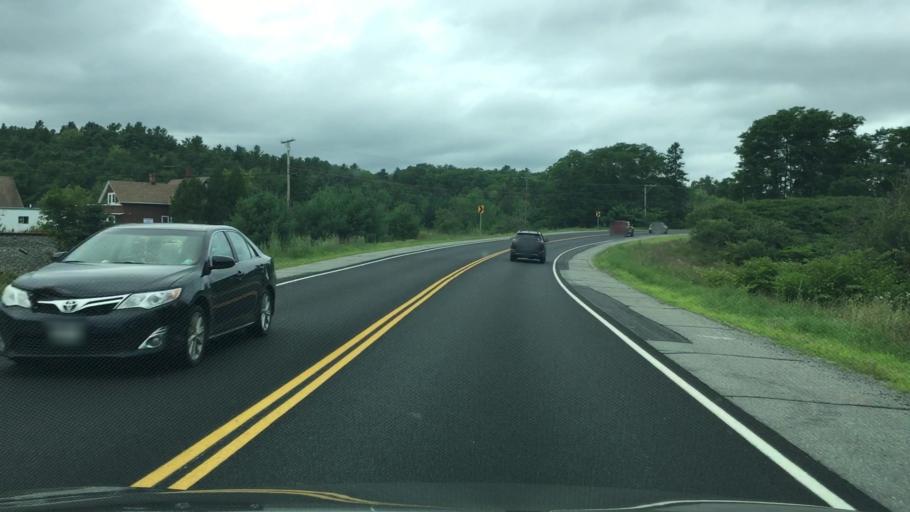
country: US
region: Maine
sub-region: Penobscot County
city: Orrington
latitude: 44.6969
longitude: -68.8182
